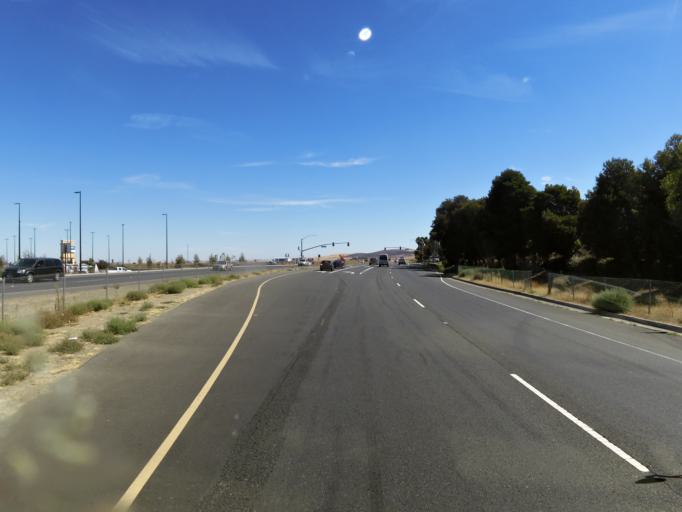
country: US
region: California
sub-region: Solano County
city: Suisun
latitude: 38.2414
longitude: -121.9915
